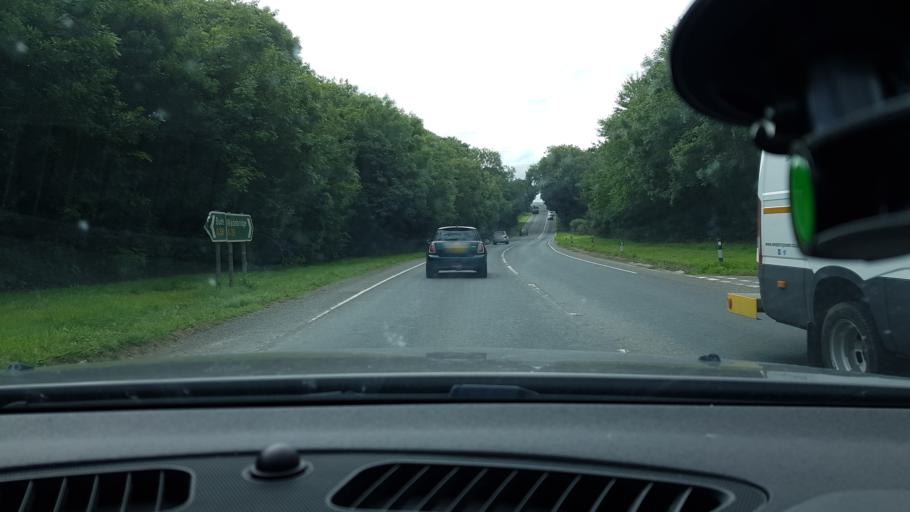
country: GB
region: England
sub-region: Cornwall
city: Helland
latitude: 50.5501
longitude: -4.7626
